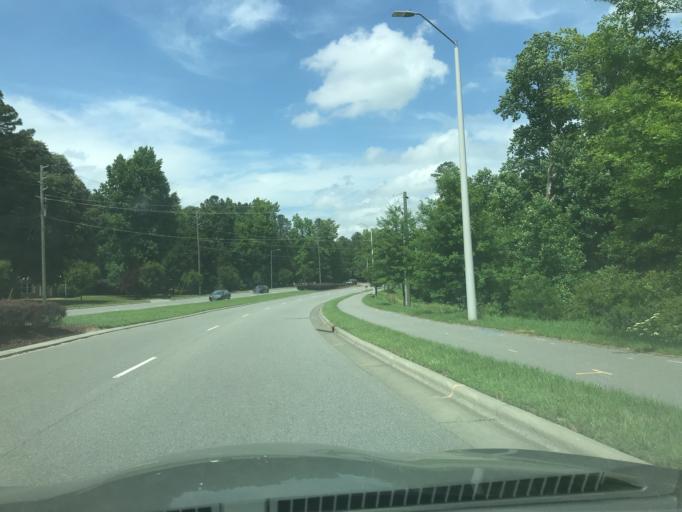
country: US
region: North Carolina
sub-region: Wake County
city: Wake Forest
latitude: 35.9275
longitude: -78.5874
